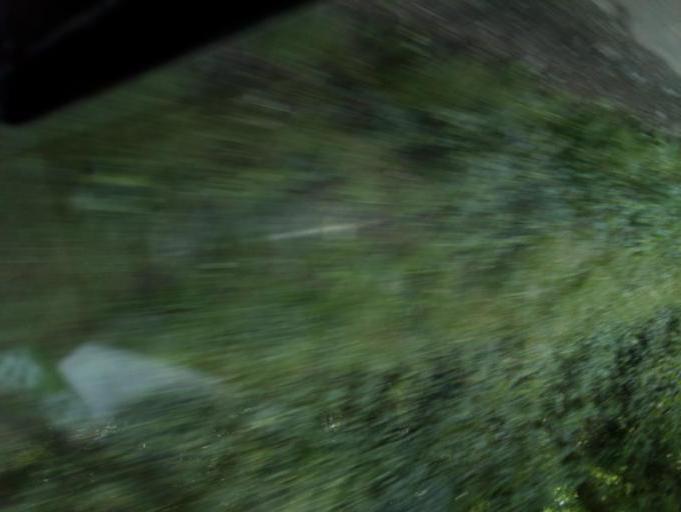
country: GB
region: England
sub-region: Gloucestershire
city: Newent
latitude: 51.8499
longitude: -2.3952
